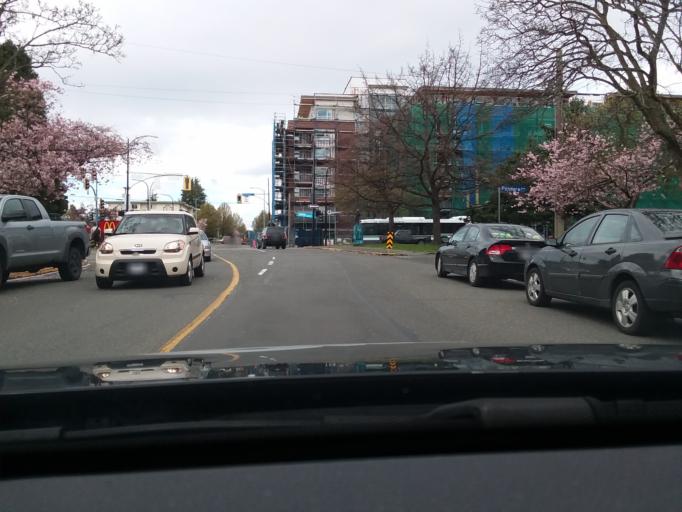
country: CA
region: British Columbia
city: Victoria
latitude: 48.4268
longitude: -123.3562
